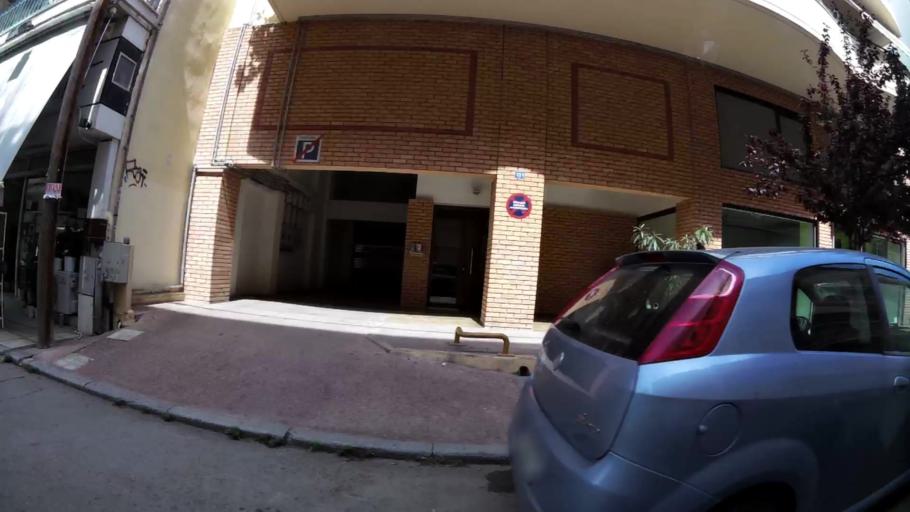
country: GR
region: Central Macedonia
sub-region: Nomos Thessalonikis
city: Triandria
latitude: 40.6057
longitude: 22.9618
